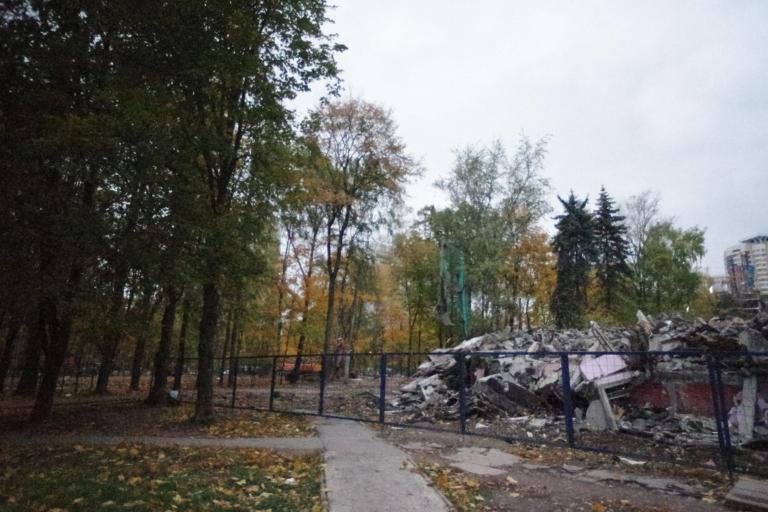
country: RU
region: Moscow
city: Troparevo
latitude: 55.6615
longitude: 37.5141
